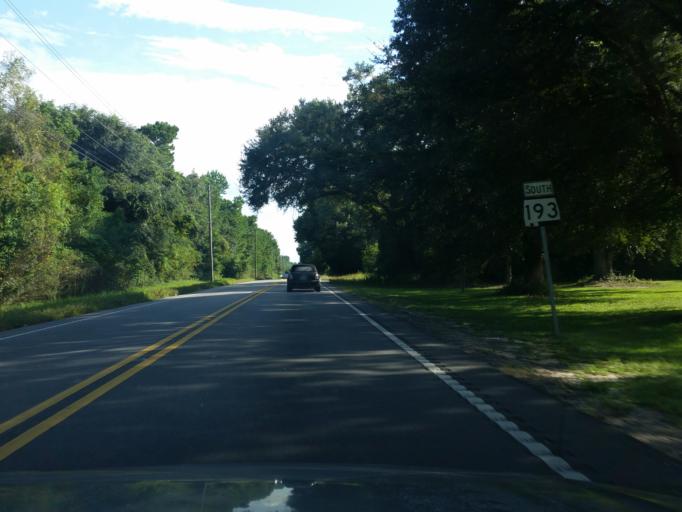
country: US
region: Alabama
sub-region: Mobile County
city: Theodore
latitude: 30.4628
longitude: -88.1149
